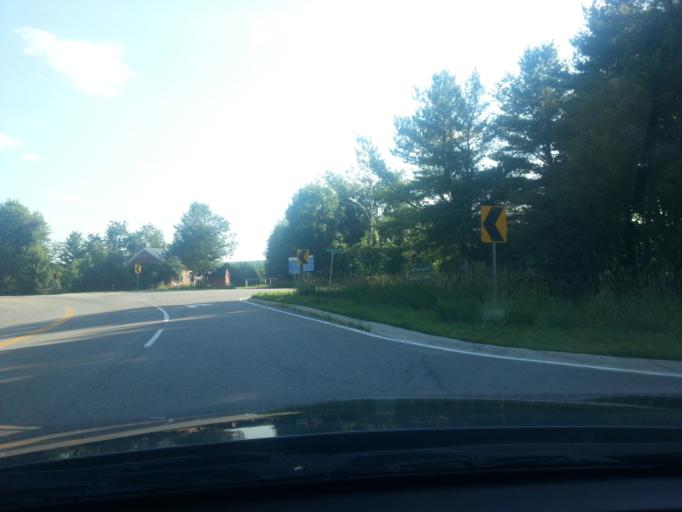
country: CA
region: Ontario
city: Carleton Place
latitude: 45.0629
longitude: -76.2854
